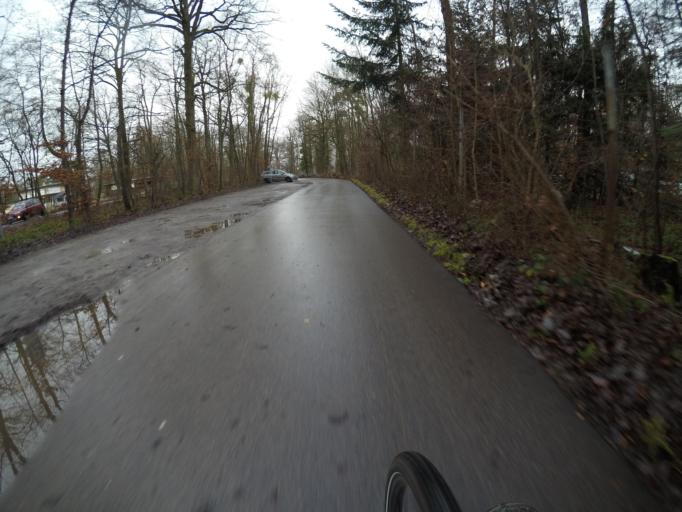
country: DE
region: Baden-Wuerttemberg
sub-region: Regierungsbezirk Stuttgart
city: Gerlingen
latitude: 48.7878
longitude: 9.0711
